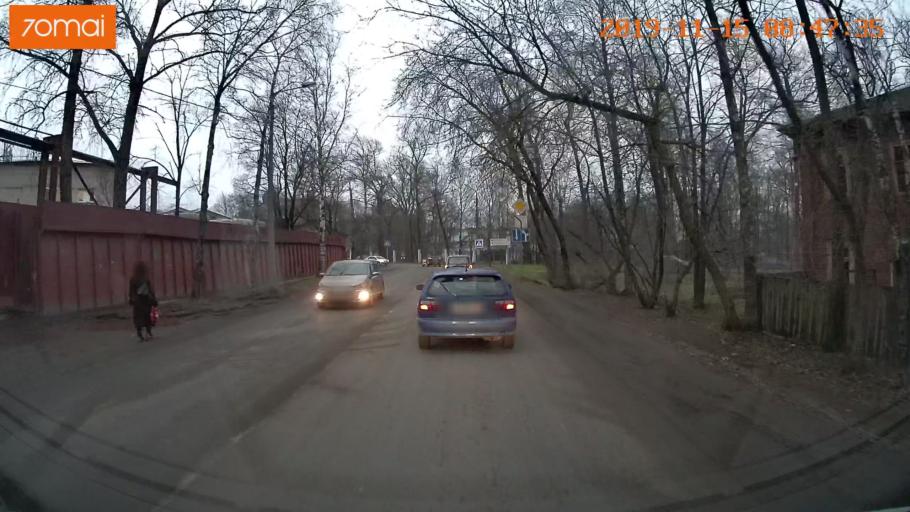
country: RU
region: Vologda
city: Cherepovets
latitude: 59.1211
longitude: 37.9171
